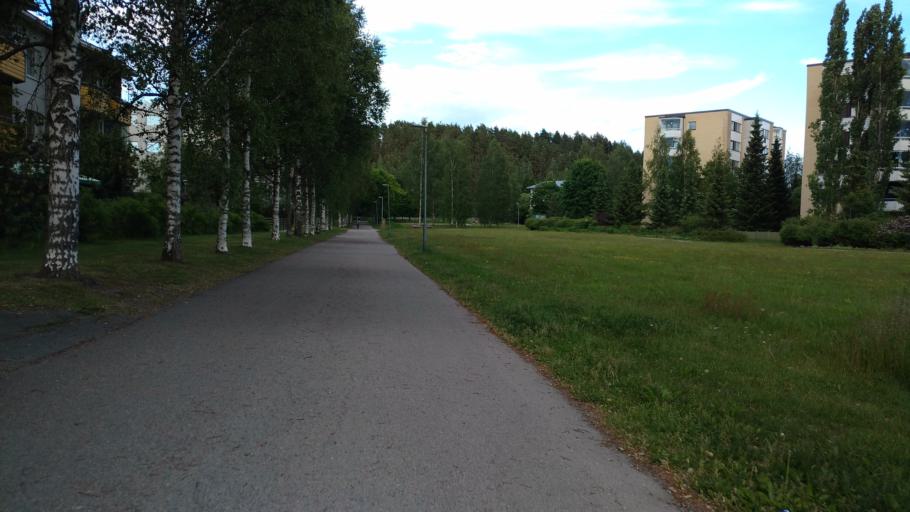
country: FI
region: Varsinais-Suomi
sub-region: Salo
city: Salo
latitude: 60.3846
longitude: 23.1445
